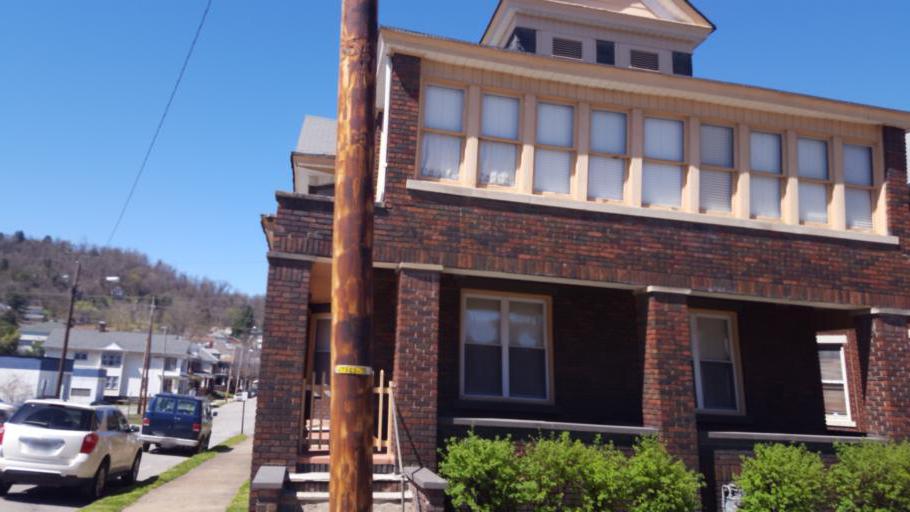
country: US
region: Ohio
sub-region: Belmont County
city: Martins Ferry
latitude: 40.0981
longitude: -80.7230
